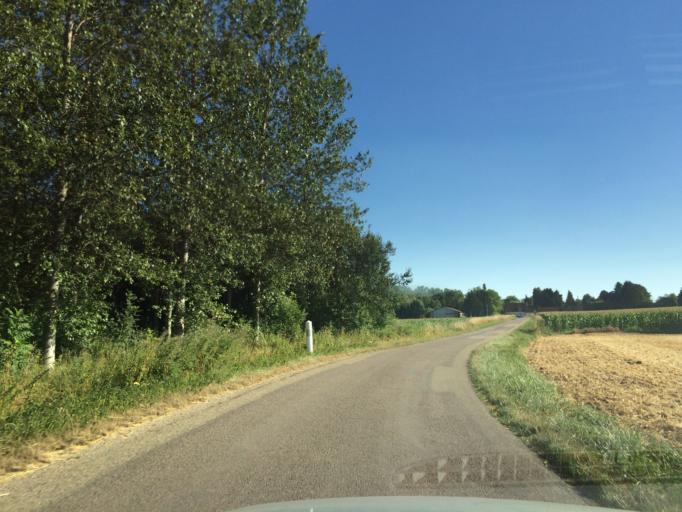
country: FR
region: Bourgogne
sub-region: Departement de l'Yonne
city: Fleury-la-Vallee
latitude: 47.9068
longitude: 3.4430
